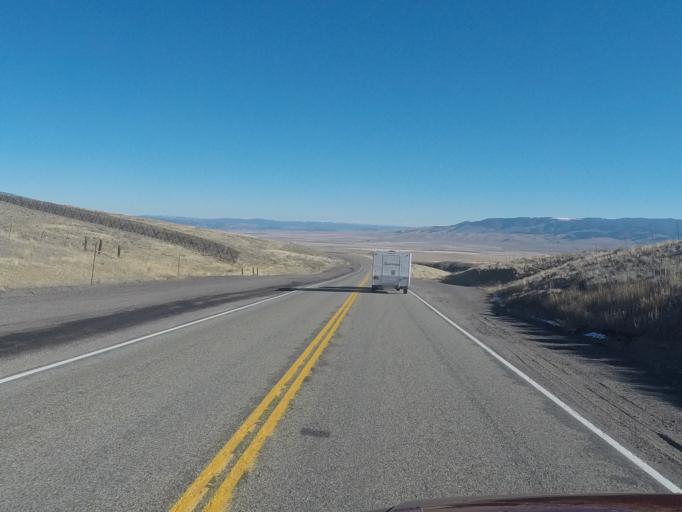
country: US
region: Montana
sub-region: Meagher County
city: White Sulphur Springs
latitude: 46.3779
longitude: -110.9909
